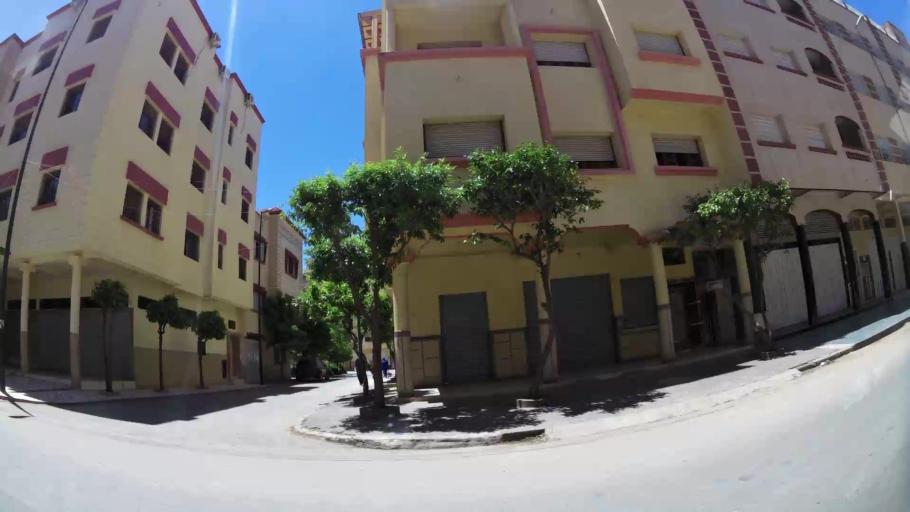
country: MA
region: Meknes-Tafilalet
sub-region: Meknes
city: Meknes
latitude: 33.8596
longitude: -5.5731
